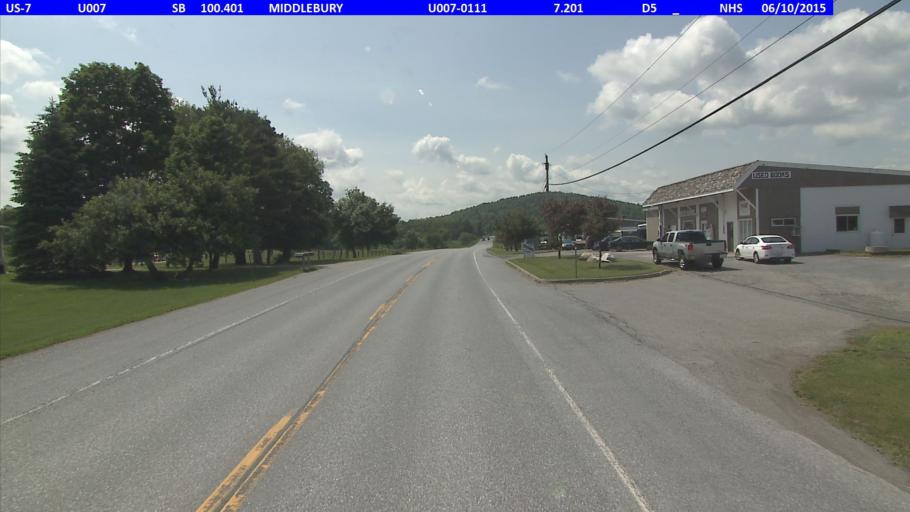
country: US
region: Vermont
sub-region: Addison County
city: Middlebury (village)
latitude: 44.0442
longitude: -73.1626
